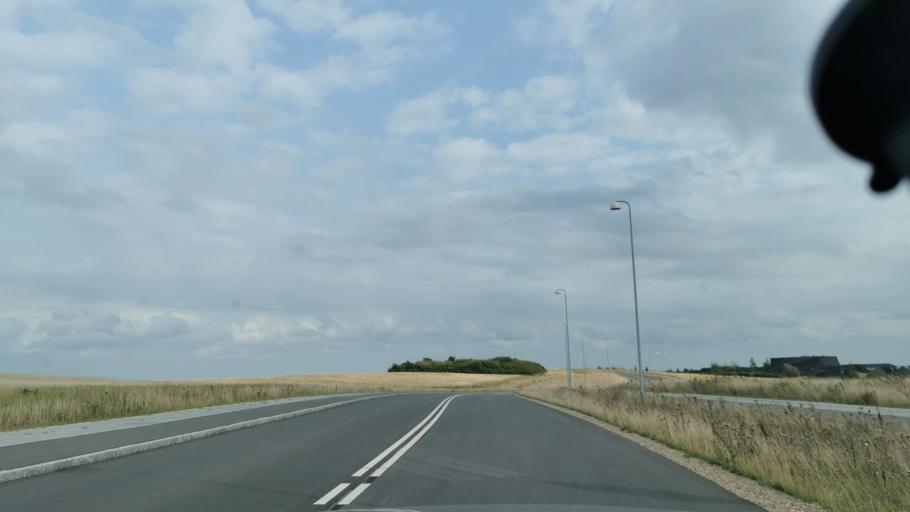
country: DK
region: Zealand
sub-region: Kalundborg Kommune
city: Kalundborg
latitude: 55.6950
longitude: 11.0751
